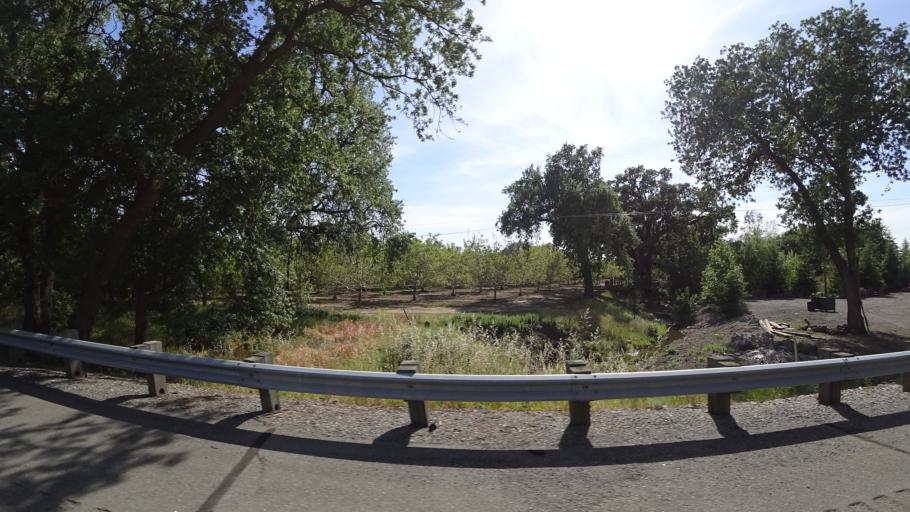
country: US
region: California
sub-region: Tehama County
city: Los Molinos
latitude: 39.9393
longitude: -122.0453
